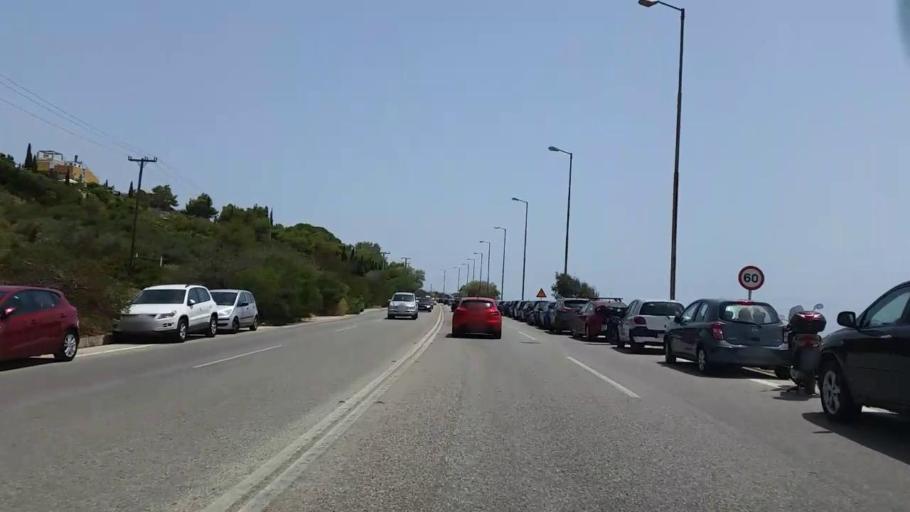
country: GR
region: Attica
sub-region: Nomarchia Anatolikis Attikis
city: Saronida
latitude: 37.7235
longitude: 23.9085
